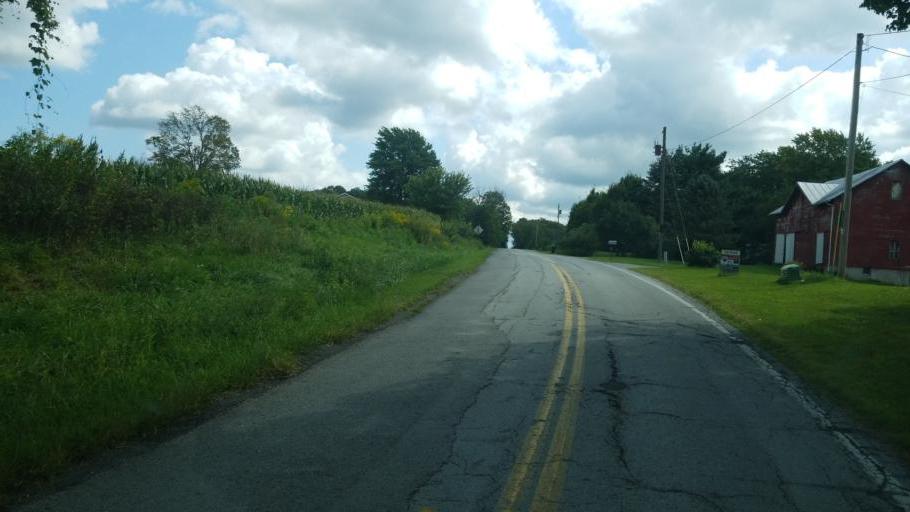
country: US
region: Ohio
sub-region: Huron County
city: Norwalk
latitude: 41.1649
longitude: -82.6406
